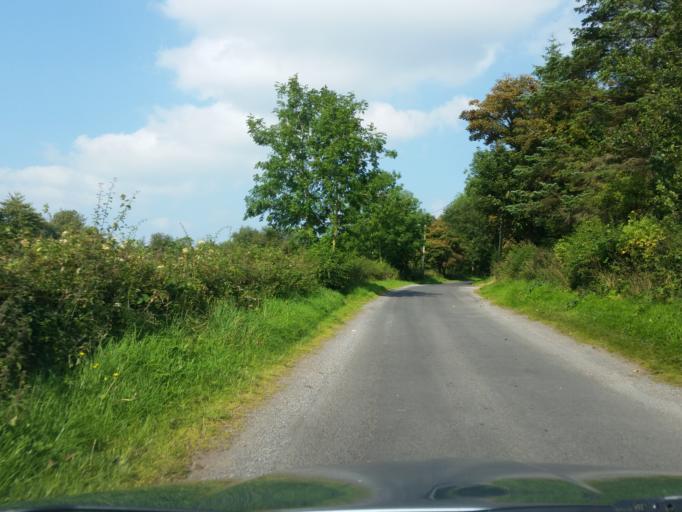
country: GB
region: Northern Ireland
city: Ballinamallard
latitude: 54.3369
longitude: -7.5357
